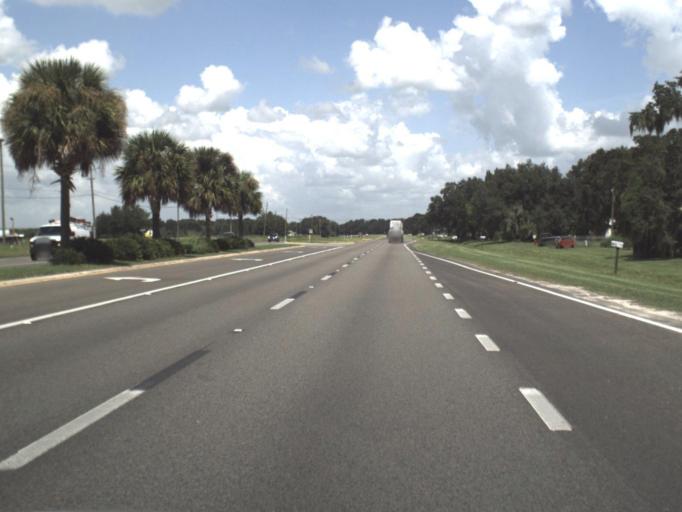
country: US
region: Florida
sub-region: Polk County
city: Fort Meade
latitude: 27.7676
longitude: -81.8013
